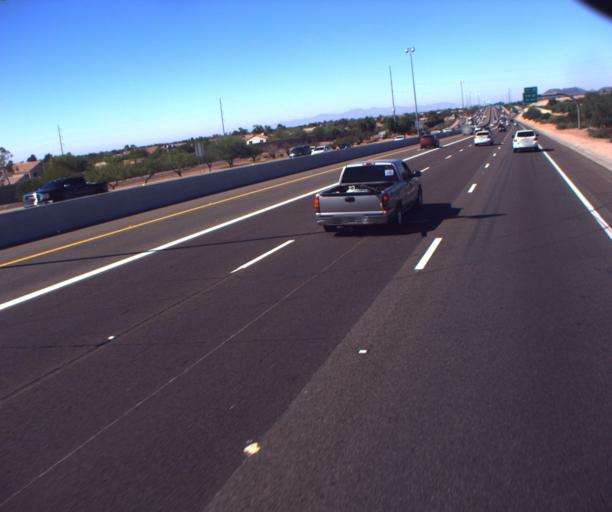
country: US
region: Arizona
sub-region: Maricopa County
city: Paradise Valley
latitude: 33.6692
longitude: -112.0529
